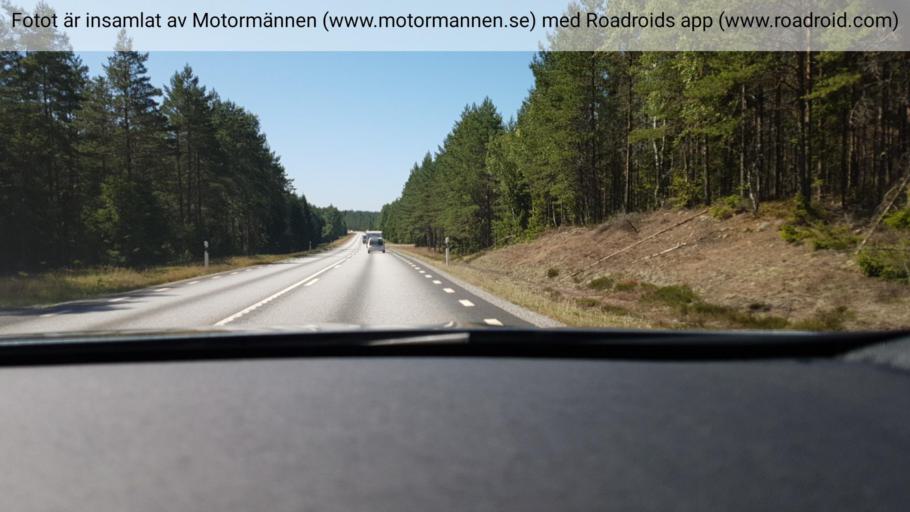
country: SE
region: Joenkoeping
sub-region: Gnosjo Kommun
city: Gnosjoe
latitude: 57.5652
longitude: 13.7012
